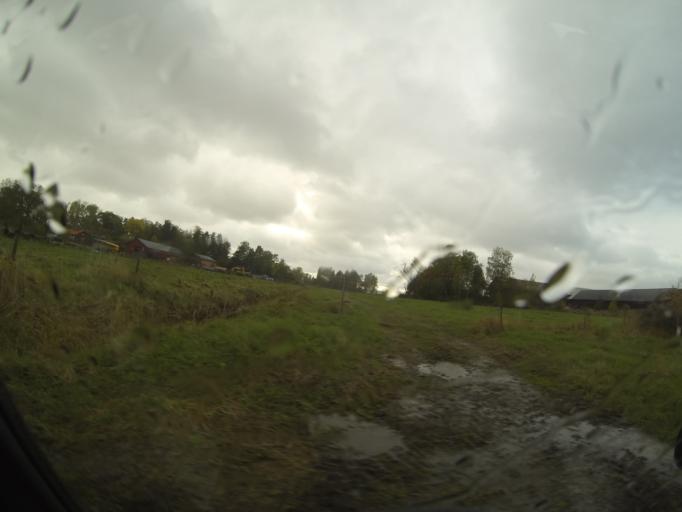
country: SE
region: Soedermanland
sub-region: Eskilstuna Kommun
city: Kvicksund
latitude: 59.3406
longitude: 16.2990
